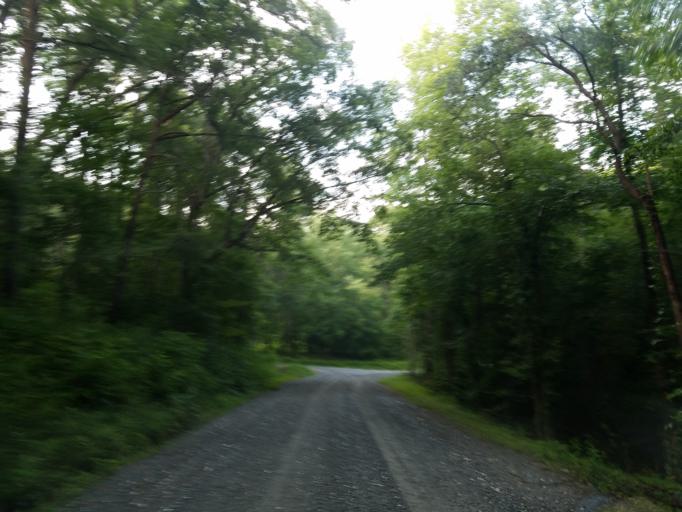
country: US
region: Georgia
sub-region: Pickens County
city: Jasper
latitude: 34.5476
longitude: -84.4437
